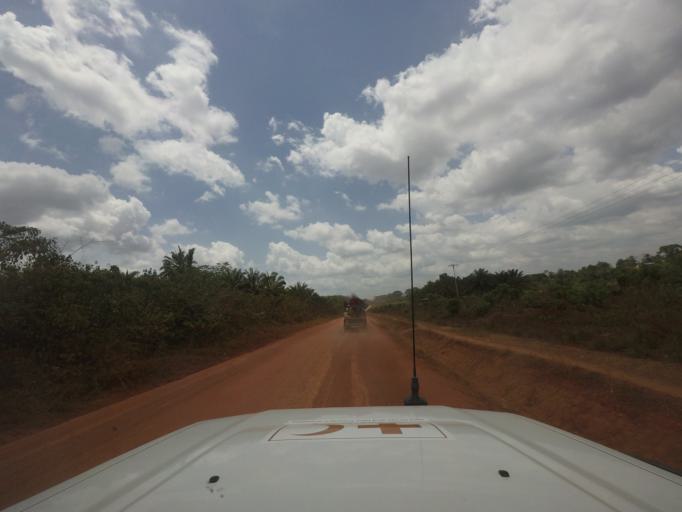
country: LR
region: Nimba
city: Sanniquellie
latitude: 7.2318
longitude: -8.9553
